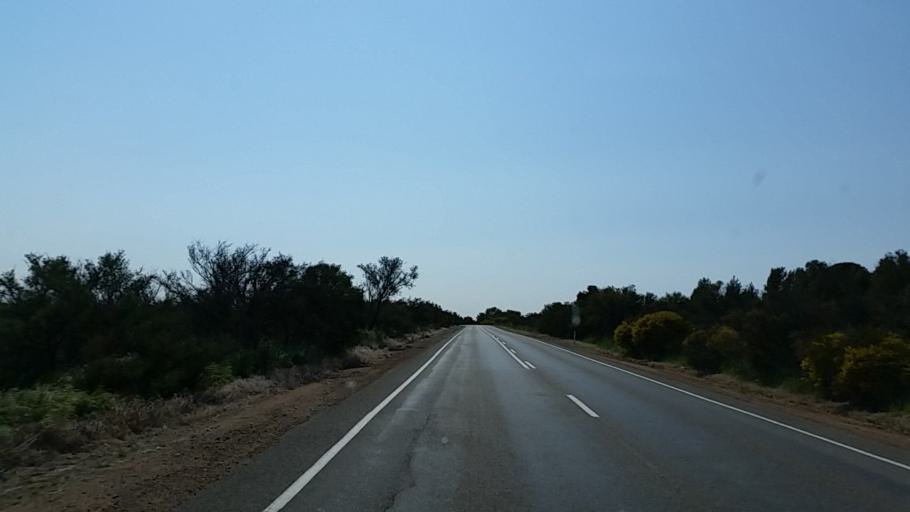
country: AU
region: South Australia
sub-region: Port Pirie City and Dists
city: Crystal Brook
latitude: -33.2366
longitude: 138.3880
